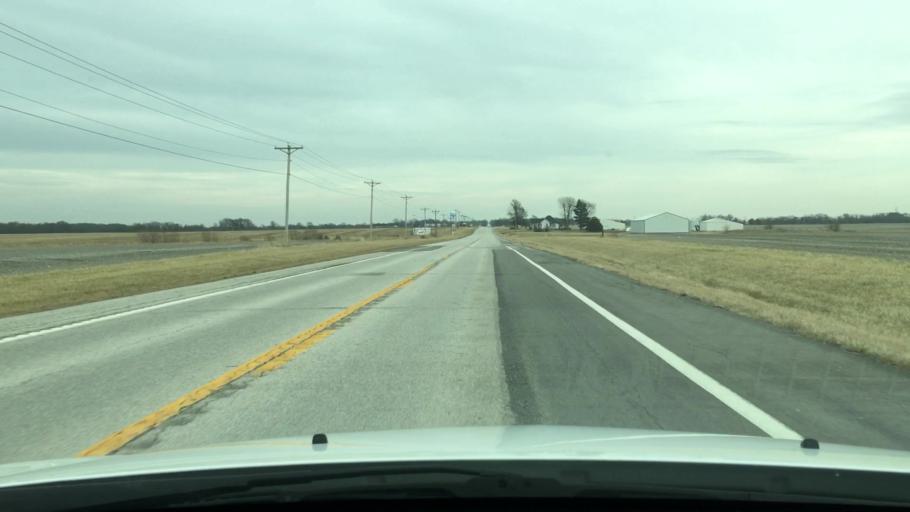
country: US
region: Missouri
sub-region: Audrain County
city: Vandalia
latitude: 39.3459
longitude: -91.3712
